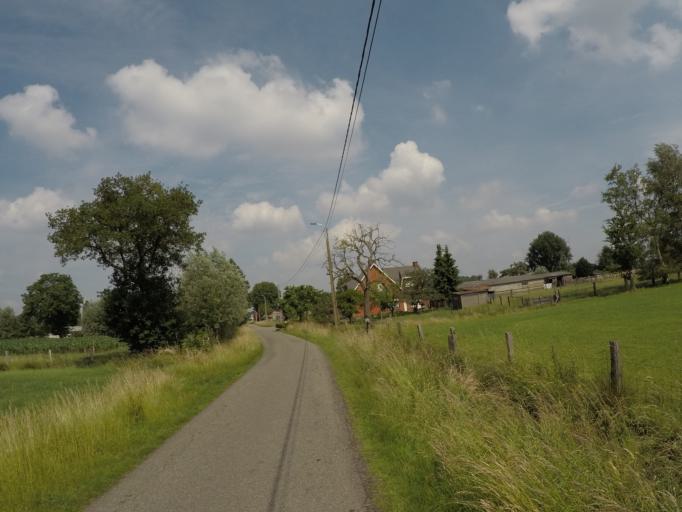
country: BE
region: Flanders
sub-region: Provincie Antwerpen
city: Brecht
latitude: 51.3364
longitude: 4.5907
